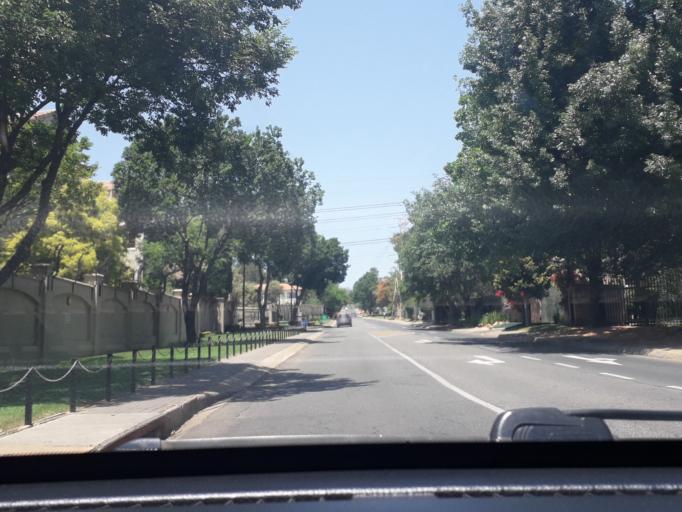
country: ZA
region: Gauteng
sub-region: City of Johannesburg Metropolitan Municipality
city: Modderfontein
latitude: -26.0847
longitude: 28.0513
